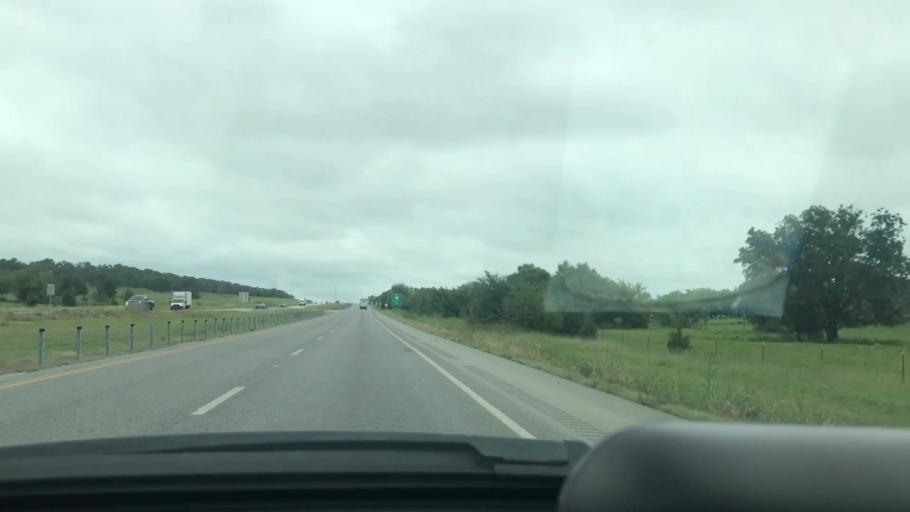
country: US
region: Oklahoma
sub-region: Coal County
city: Coalgate
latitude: 34.6635
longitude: -95.9386
